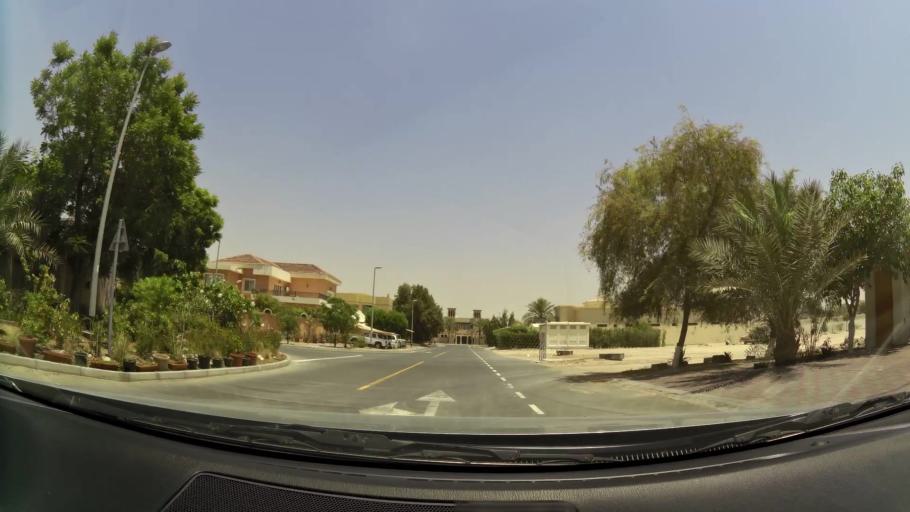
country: AE
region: Dubai
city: Dubai
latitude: 25.0968
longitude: 55.1975
